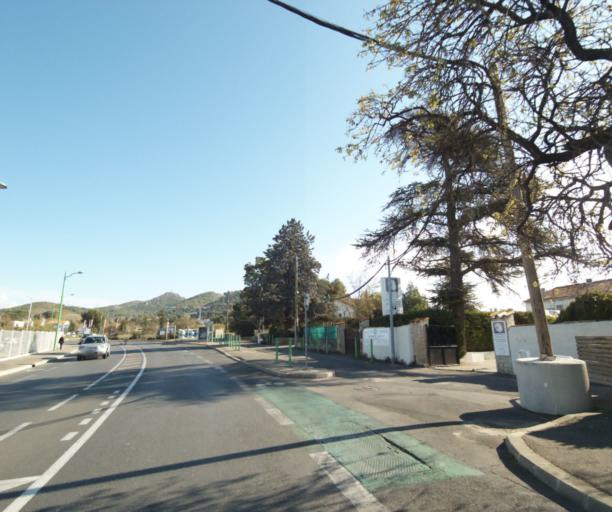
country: FR
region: Provence-Alpes-Cote d'Azur
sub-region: Departement des Bouches-du-Rhone
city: Allauch
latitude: 43.3377
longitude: 5.4726
